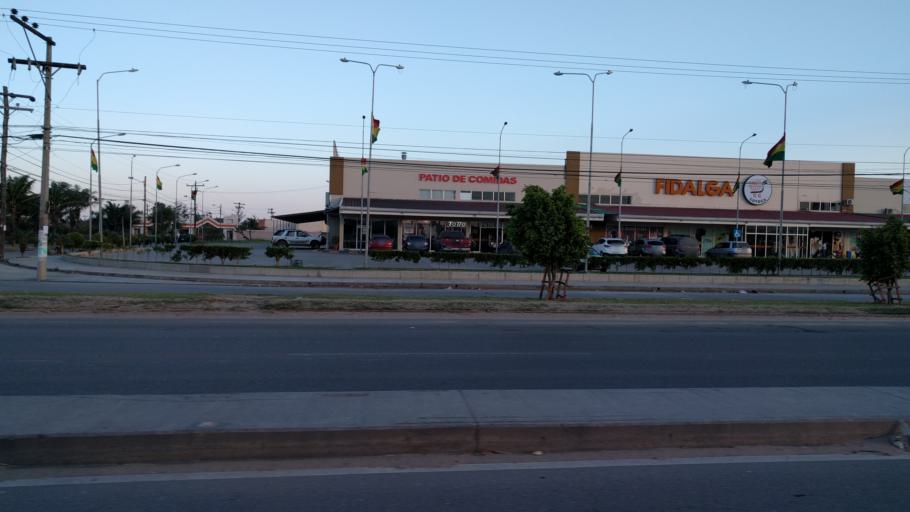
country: BO
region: Santa Cruz
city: Cotoca
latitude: -17.7651
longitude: -63.1042
